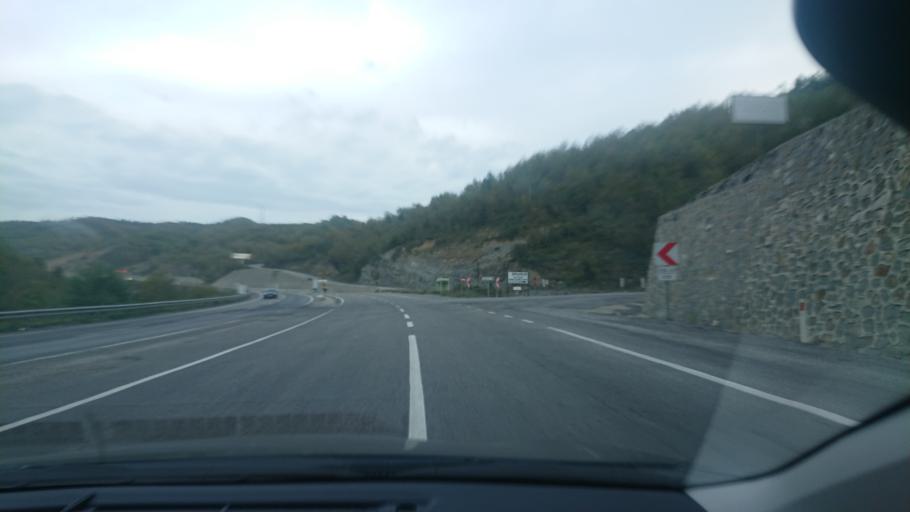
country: TR
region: Zonguldak
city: Beycuma
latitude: 41.4056
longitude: 31.9363
